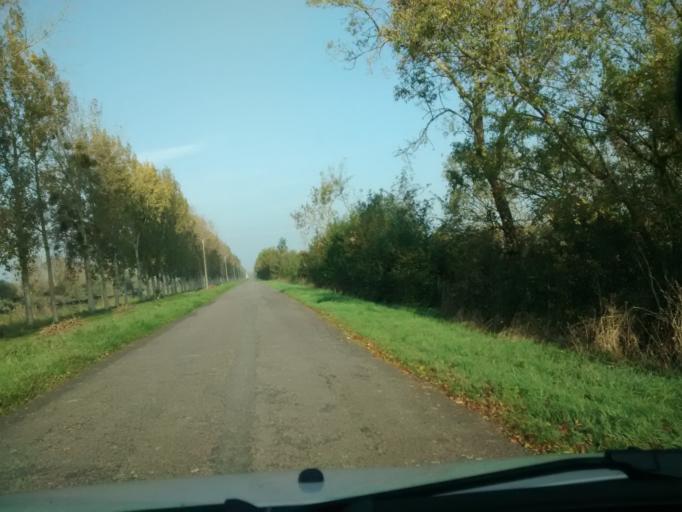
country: FR
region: Pays de la Loire
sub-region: Departement de la Loire-Atlantique
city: Vue
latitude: 47.2283
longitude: -1.8502
